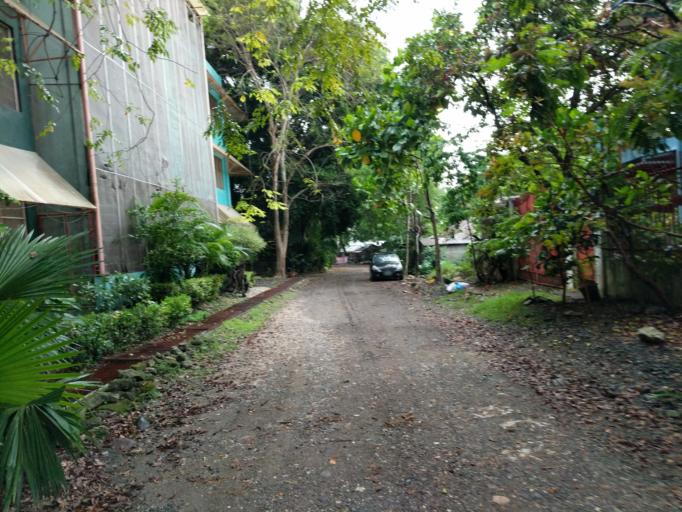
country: PH
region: Davao
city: Davao
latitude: 7.0783
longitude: 125.5820
